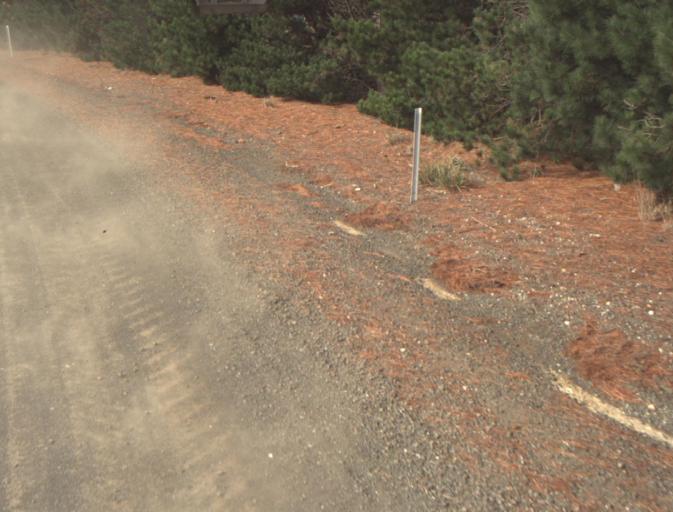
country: AU
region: Tasmania
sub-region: Launceston
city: Mayfield
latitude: -41.2108
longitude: 147.1838
